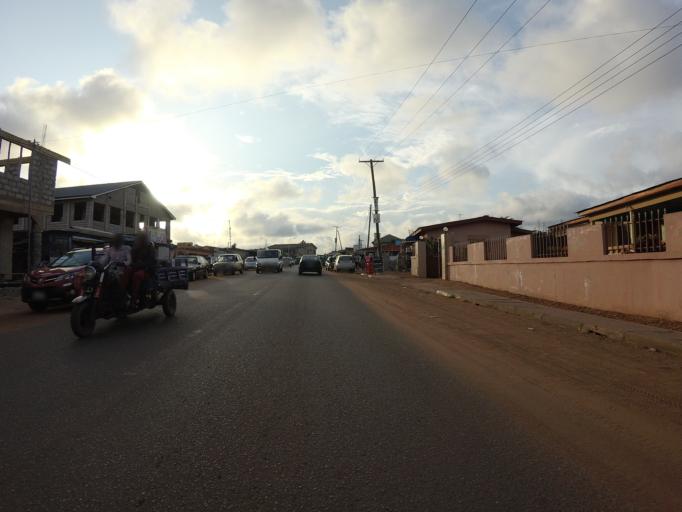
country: GH
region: Greater Accra
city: Teshi Old Town
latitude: 5.5964
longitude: -0.1249
